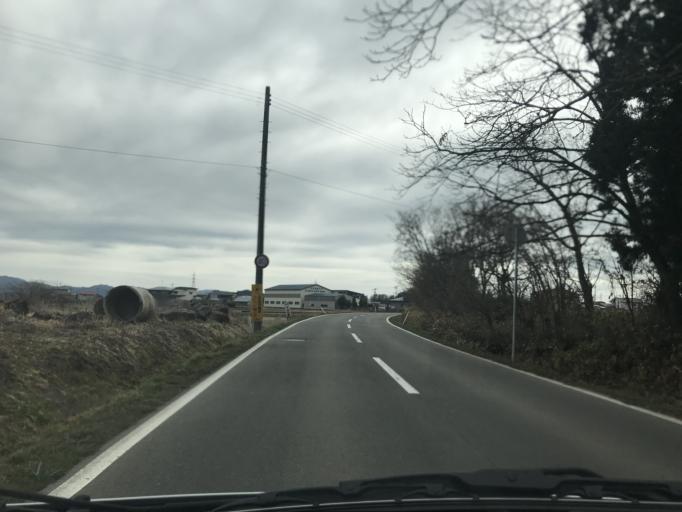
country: JP
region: Iwate
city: Hanamaki
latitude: 39.3597
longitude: 141.1317
